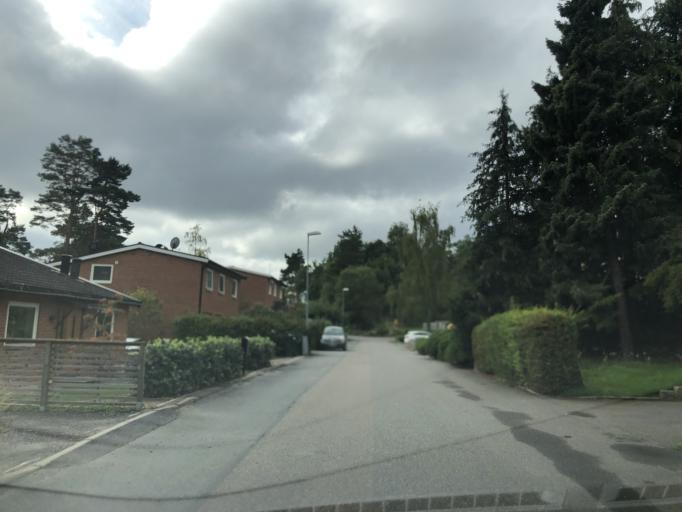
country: SE
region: Vaestra Goetaland
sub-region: Goteborg
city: Majorna
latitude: 57.7399
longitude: 11.9116
